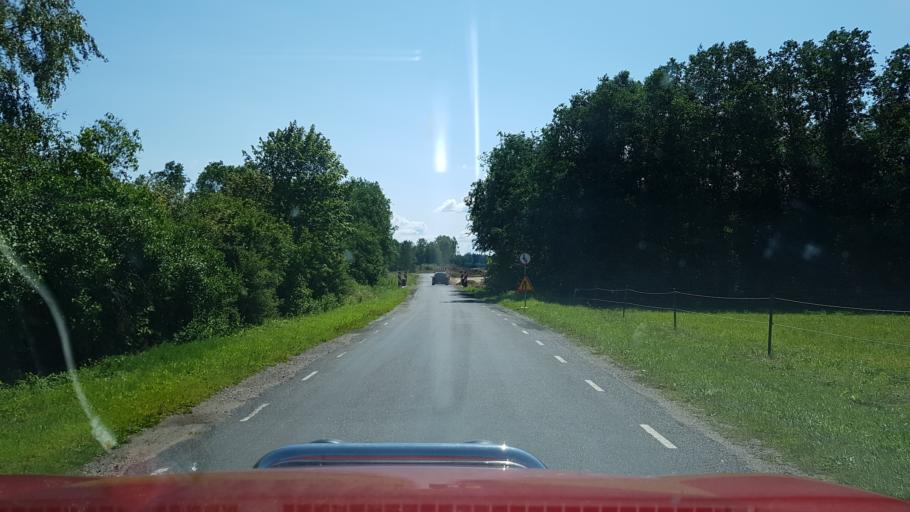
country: EE
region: Harju
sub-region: Saue linn
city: Saue
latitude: 59.1614
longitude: 24.5032
